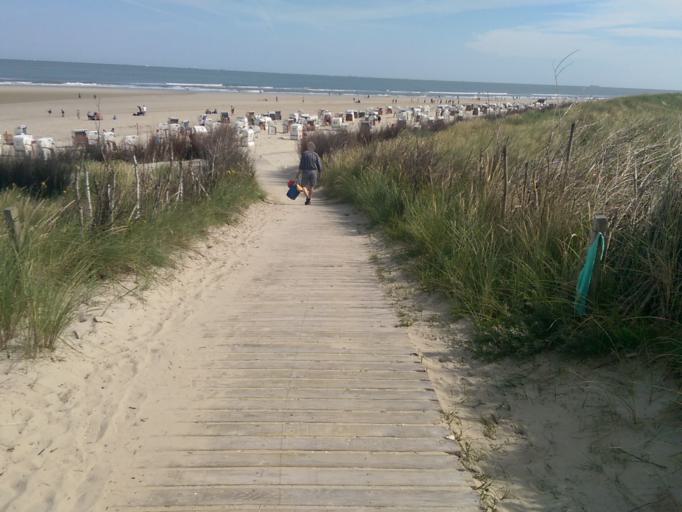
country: DE
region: Lower Saxony
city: Spiekeroog
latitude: 53.7784
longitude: 7.6910
